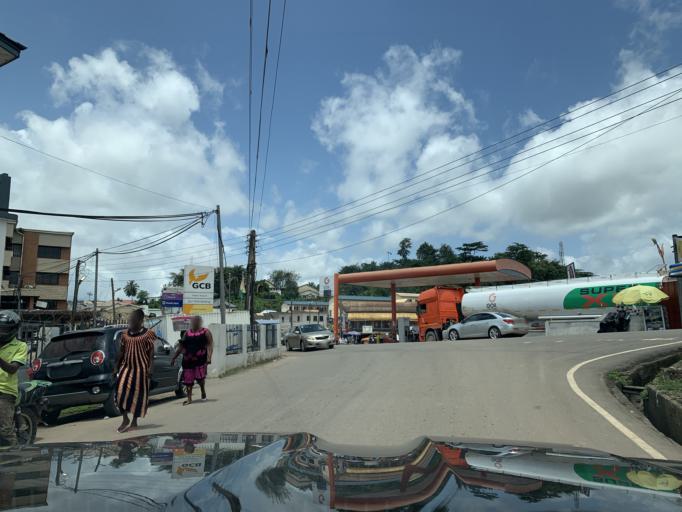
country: GH
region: Western
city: Tarkwa
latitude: 5.3044
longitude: -1.9915
